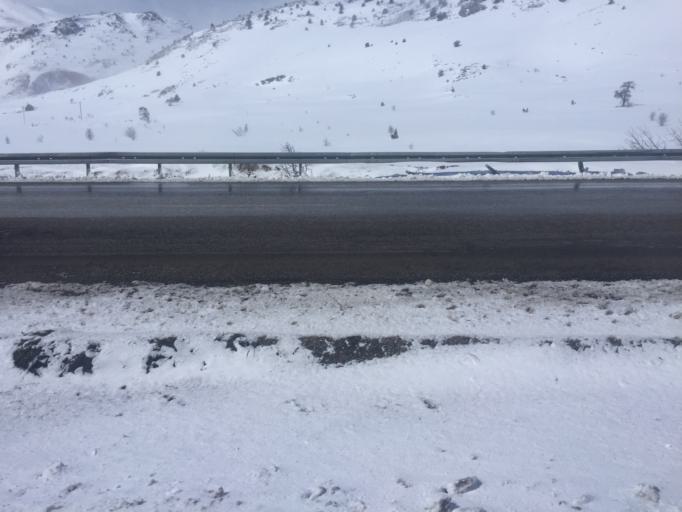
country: TR
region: Kahramanmaras
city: Goksun
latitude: 38.1849
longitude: 36.4563
